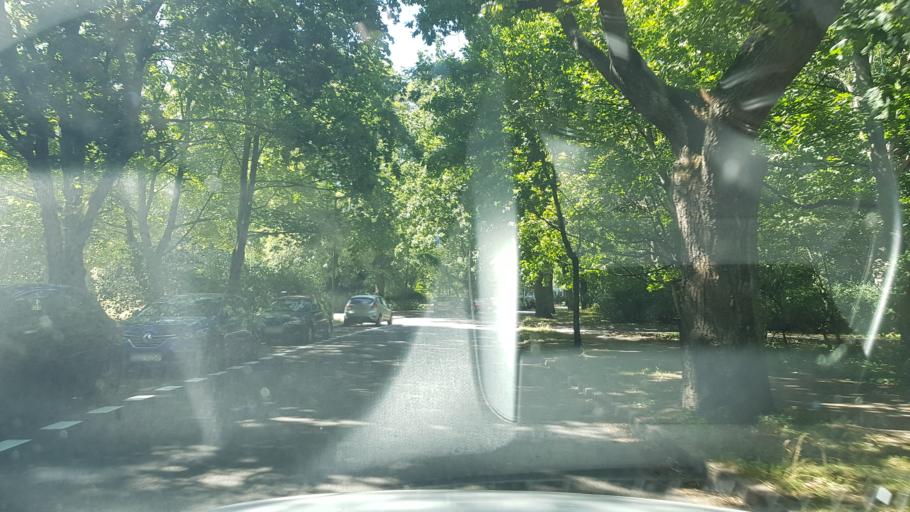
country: PL
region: West Pomeranian Voivodeship
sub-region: Szczecin
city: Szczecin
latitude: 53.4325
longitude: 14.5618
